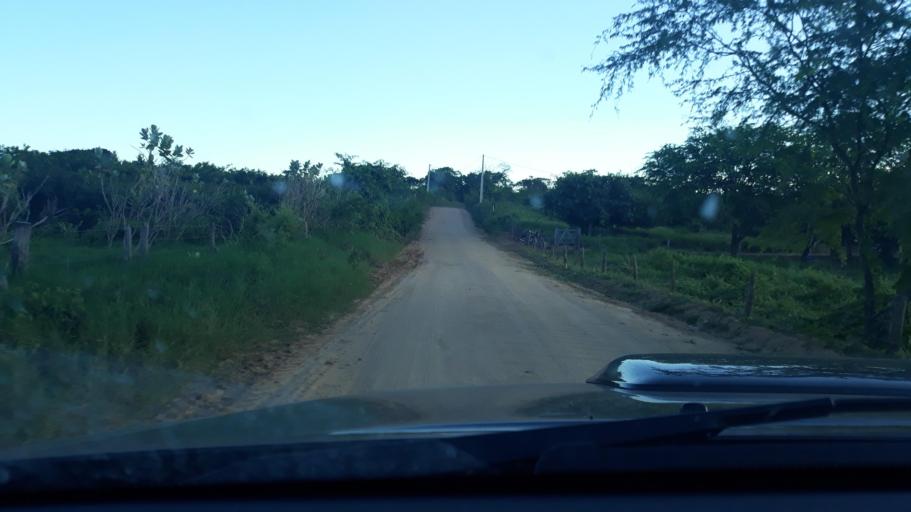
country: BR
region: Bahia
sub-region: Riacho De Santana
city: Riacho de Santana
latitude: -13.8031
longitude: -42.7124
